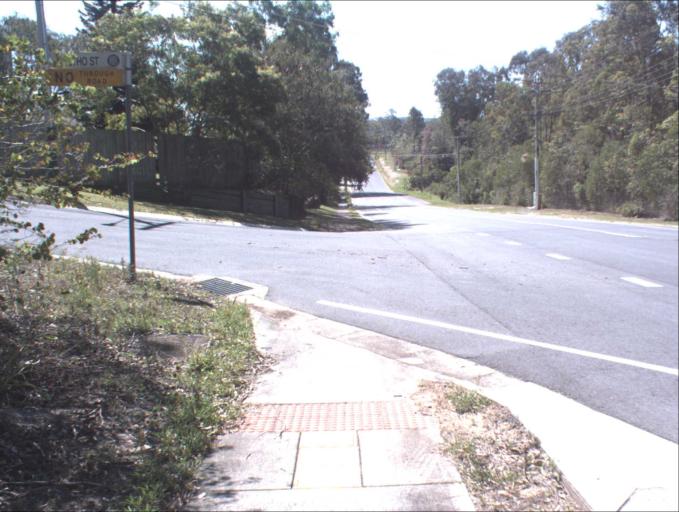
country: AU
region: Queensland
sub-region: Logan
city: Beenleigh
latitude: -27.7082
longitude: 153.1815
